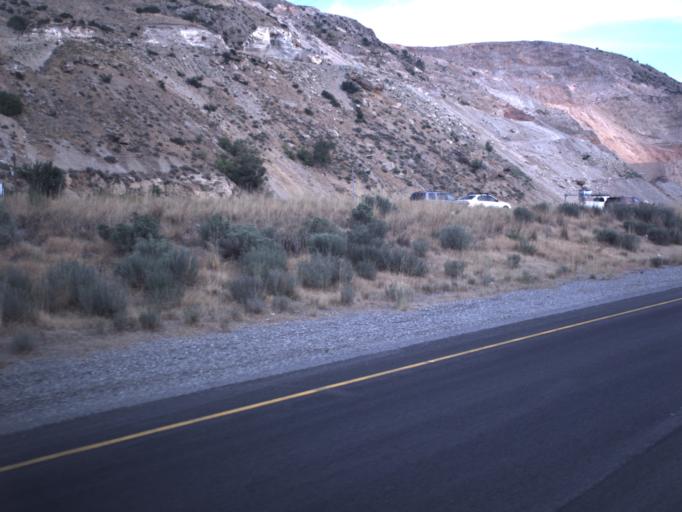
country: US
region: Utah
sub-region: Davis County
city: North Salt Lake
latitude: 40.8276
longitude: -111.9167
